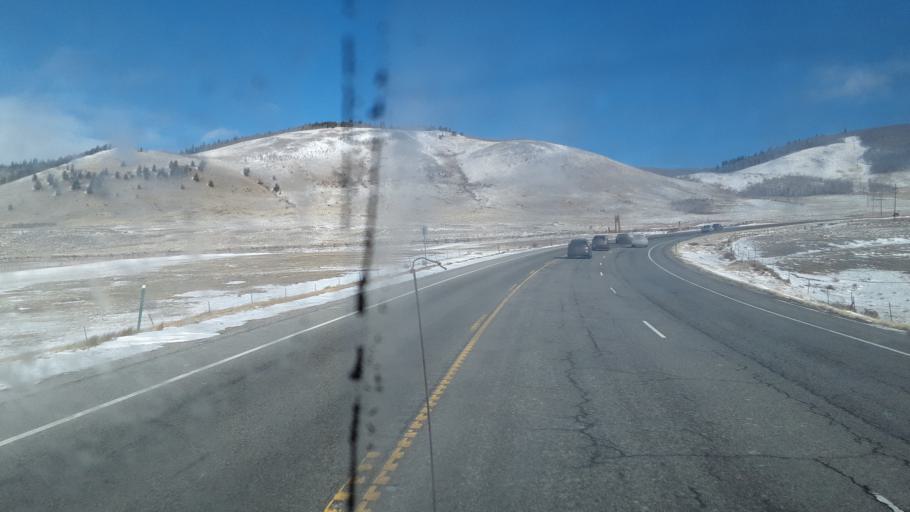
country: US
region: Colorado
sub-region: Summit County
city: Breckenridge
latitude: 39.4052
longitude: -105.7795
